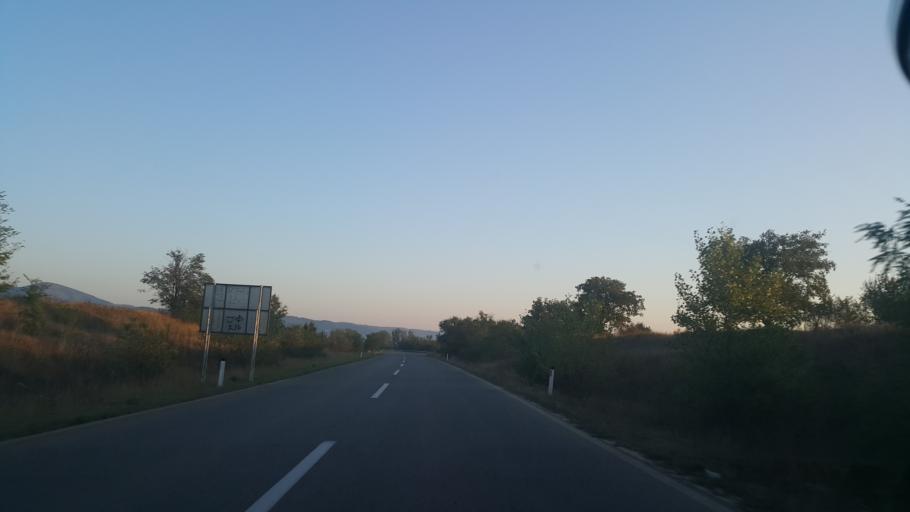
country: RS
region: Central Serbia
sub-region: Zajecarski Okrug
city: Knjazevac
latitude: 43.6385
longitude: 22.2821
